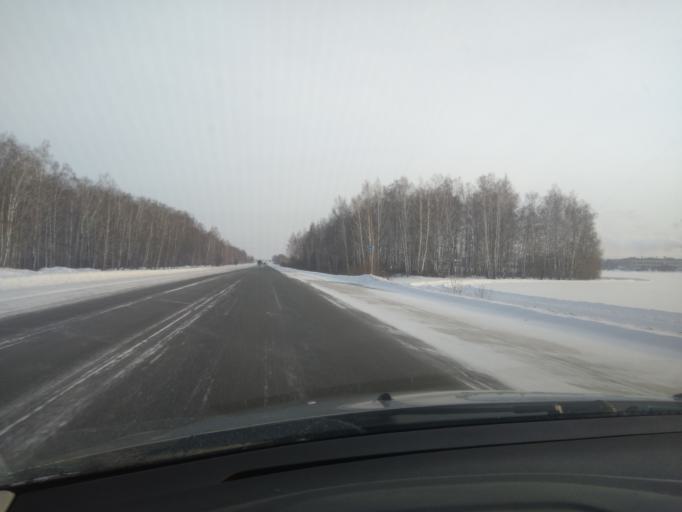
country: RU
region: Sverdlovsk
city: Bogdanovich
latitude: 56.8045
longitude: 62.0266
